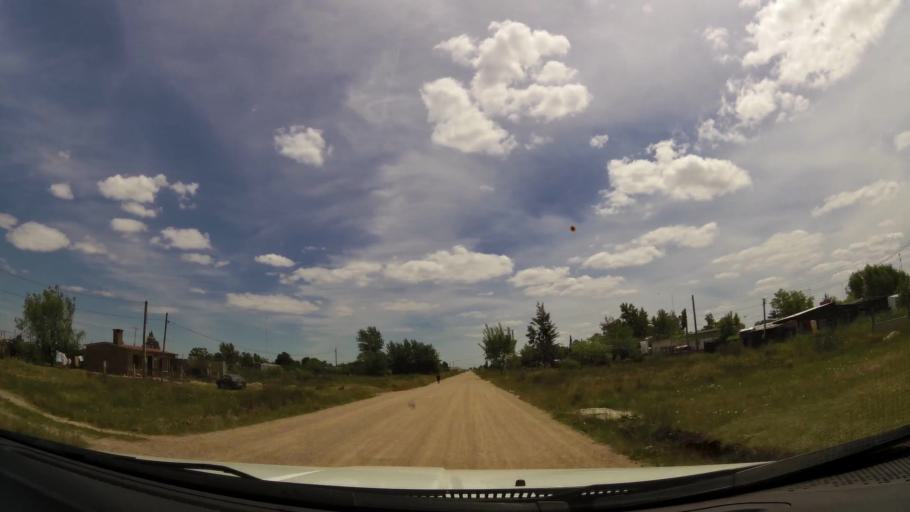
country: UY
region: San Jose
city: Delta del Tigre
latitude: -34.7615
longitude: -56.4058
